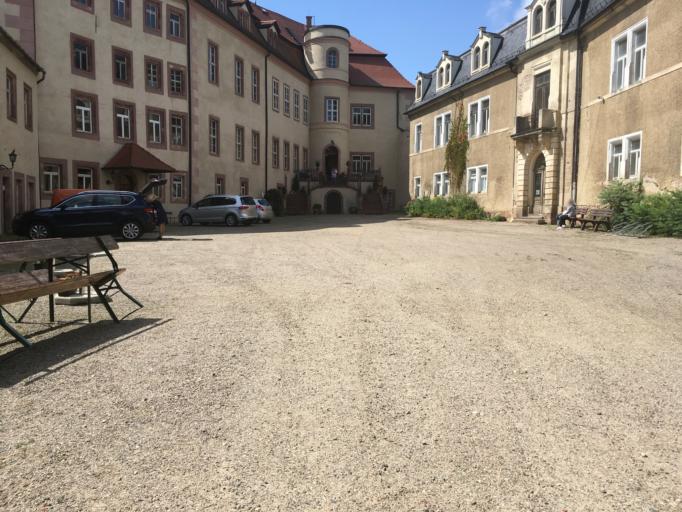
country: DE
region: Saxony
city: Niederfrohna
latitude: 50.9025
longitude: 12.6740
